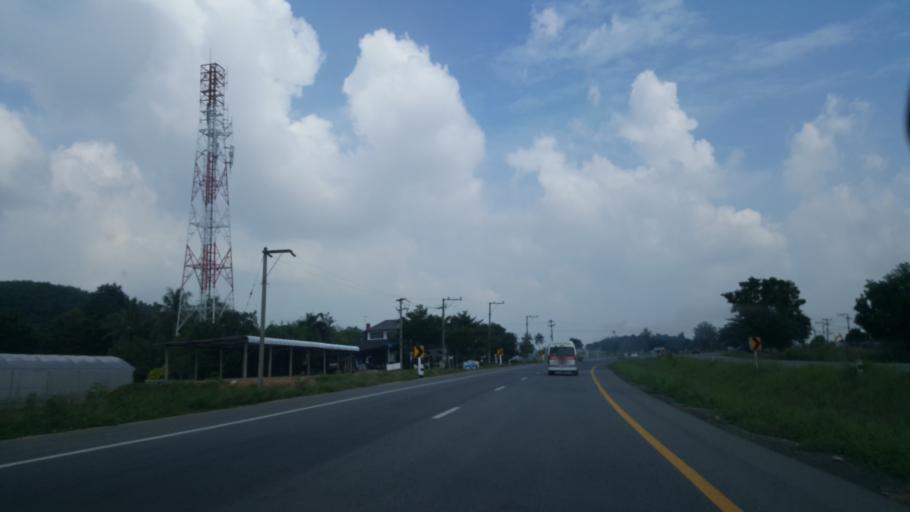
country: TH
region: Rayong
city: Ban Chang
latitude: 12.8079
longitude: 100.9922
